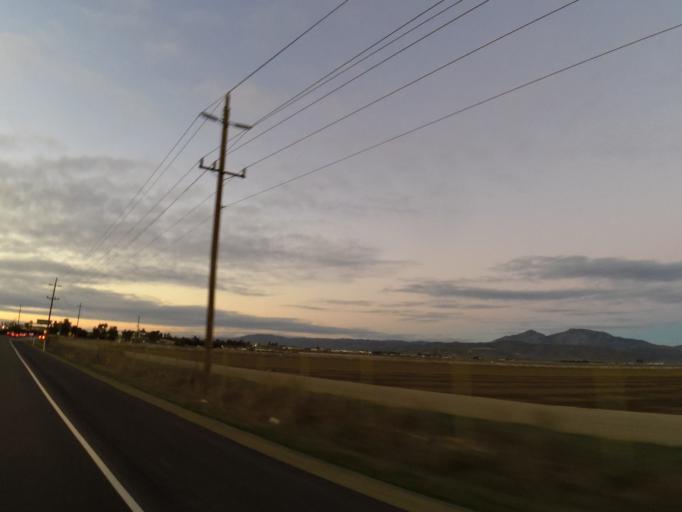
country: US
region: California
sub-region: Monterey County
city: Greenfield
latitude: 36.3093
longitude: -121.2299
